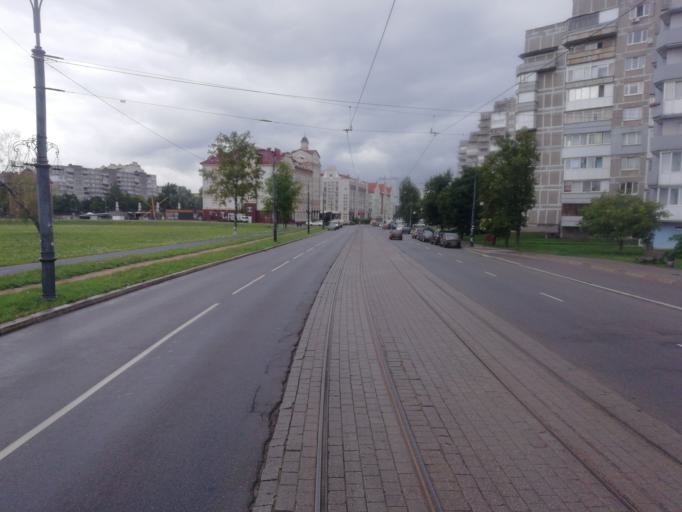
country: RU
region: Kaliningrad
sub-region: Gorod Kaliningrad
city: Kaliningrad
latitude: 54.7008
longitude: 20.5172
